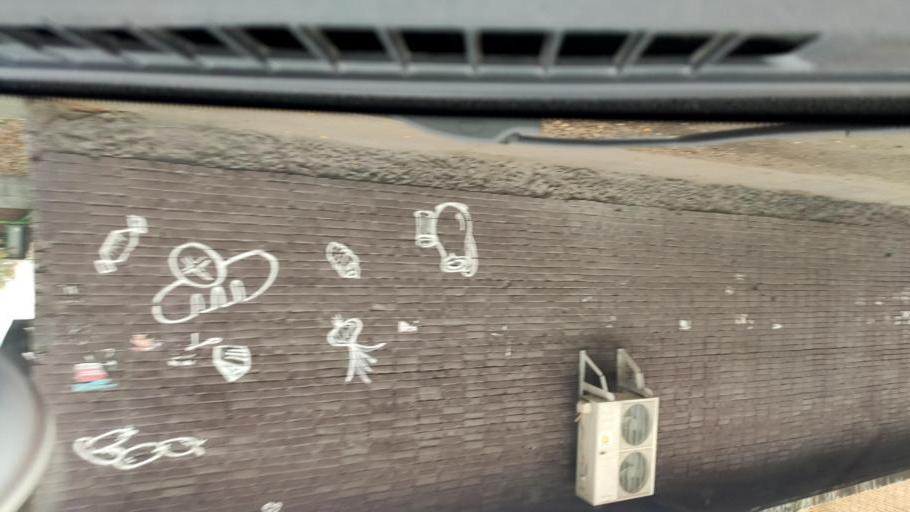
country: RU
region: Samara
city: Samara
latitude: 53.2183
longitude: 50.1545
